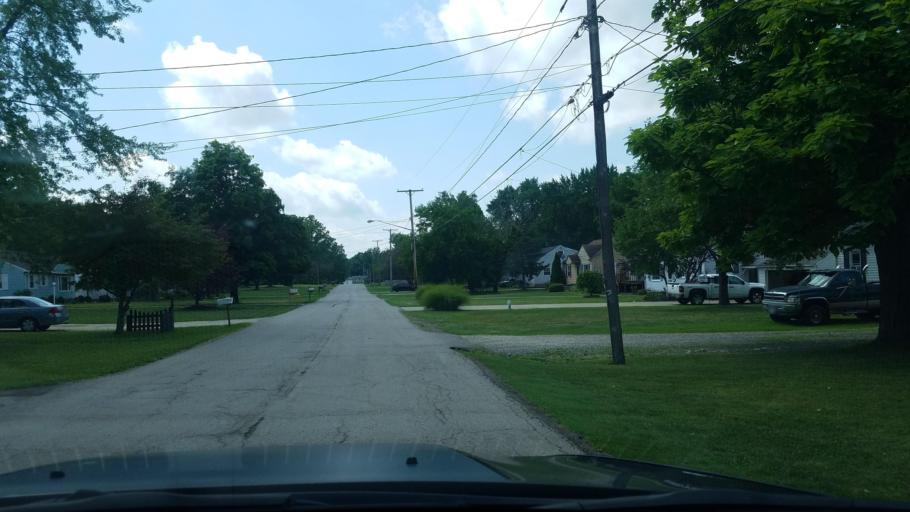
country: US
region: Ohio
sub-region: Trumbull County
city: Champion Heights
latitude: 41.2963
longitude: -80.8627
